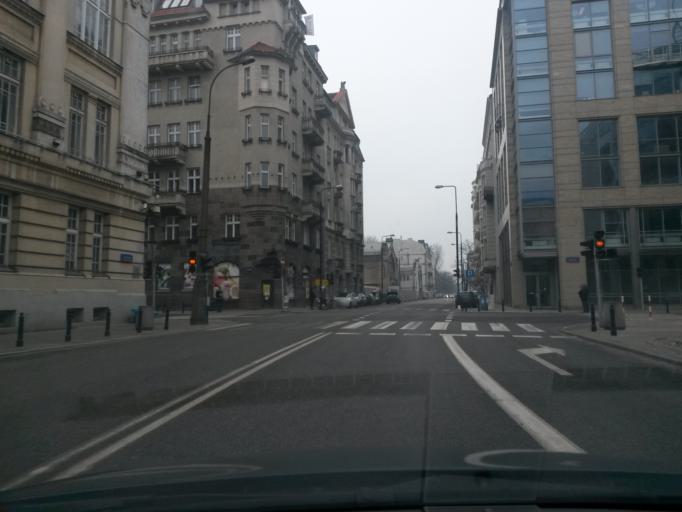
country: PL
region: Masovian Voivodeship
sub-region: Warszawa
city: Srodmiescie
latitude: 52.2226
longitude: 21.0132
